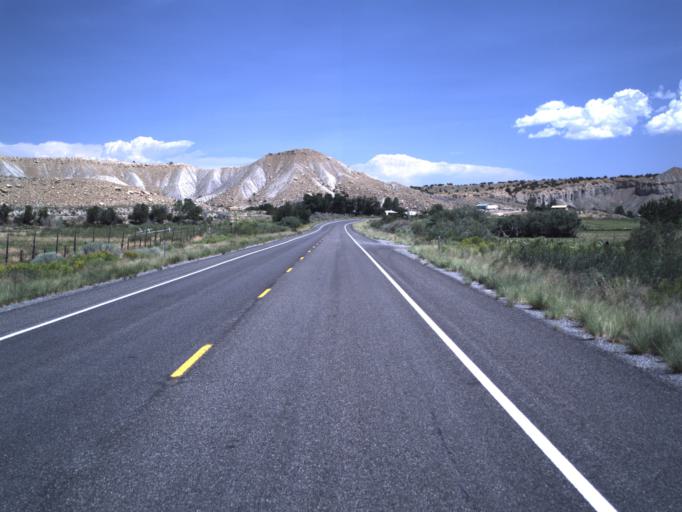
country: US
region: Utah
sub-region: Emery County
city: Huntington
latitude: 39.3622
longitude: -111.0412
